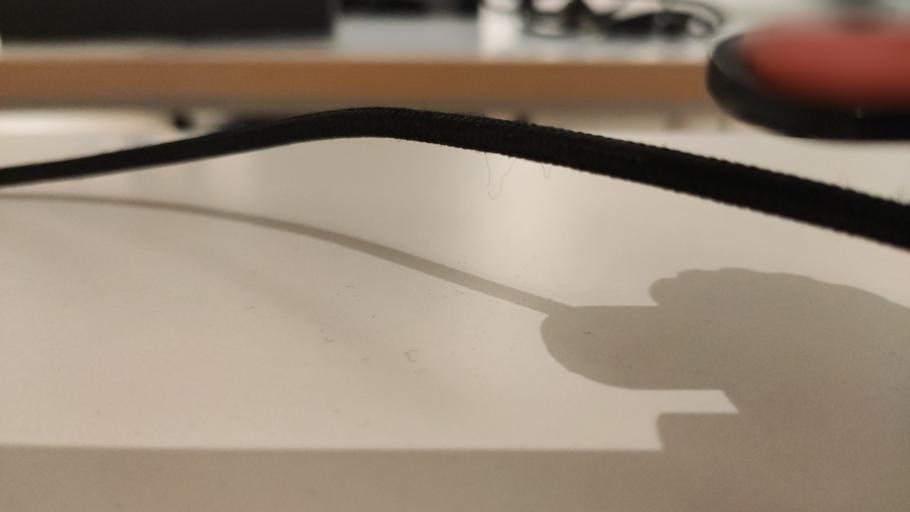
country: RU
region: Moskovskaya
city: Dorokhovo
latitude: 55.4138
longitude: 36.3686
